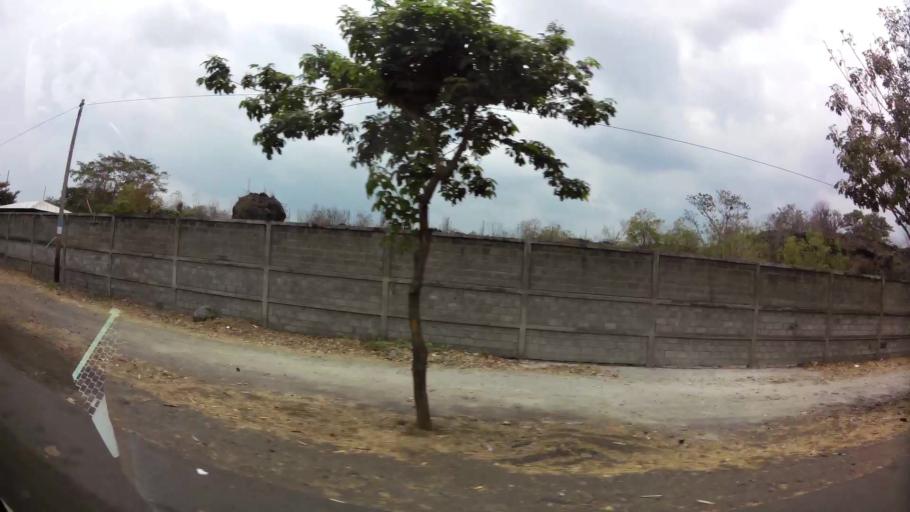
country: NI
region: Leon
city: Quezalguaque
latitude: 12.5320
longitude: -86.8933
